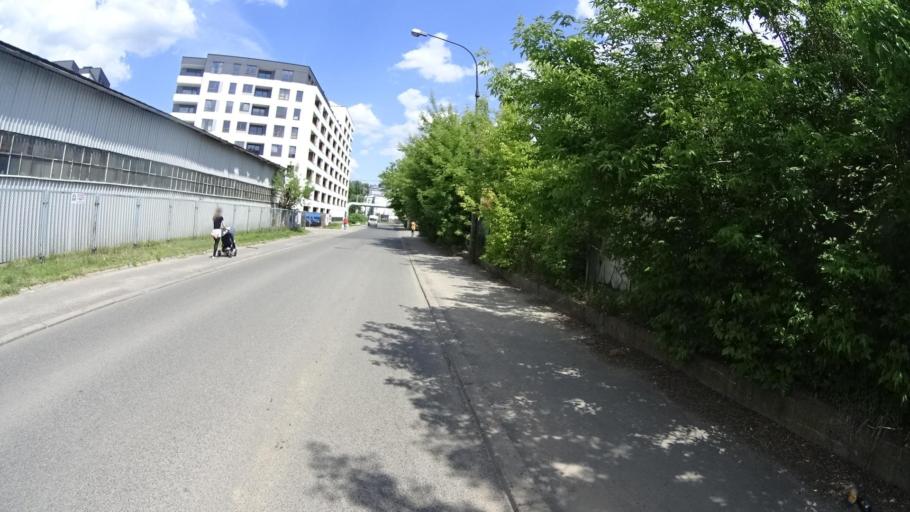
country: PL
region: Masovian Voivodeship
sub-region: Warszawa
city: Ochota
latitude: 52.2255
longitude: 20.9781
